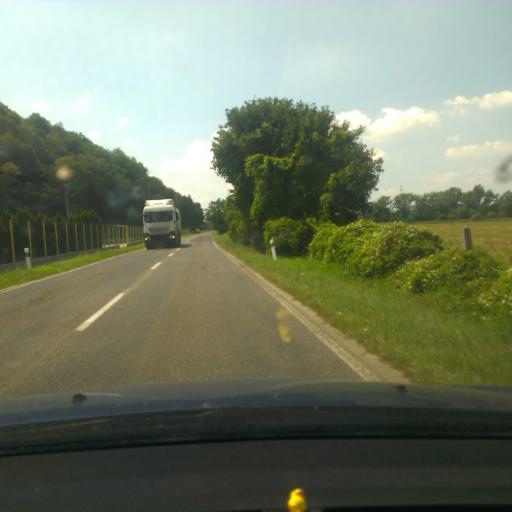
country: SK
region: Trnavsky
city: Hlohovec
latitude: 48.5049
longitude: 17.8254
